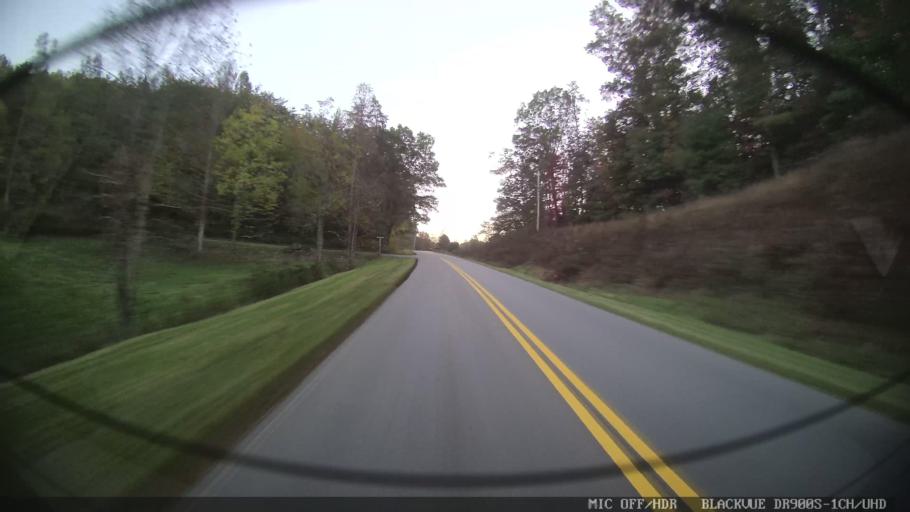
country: US
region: Georgia
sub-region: Union County
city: Blairsville
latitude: 34.8976
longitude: -83.8679
